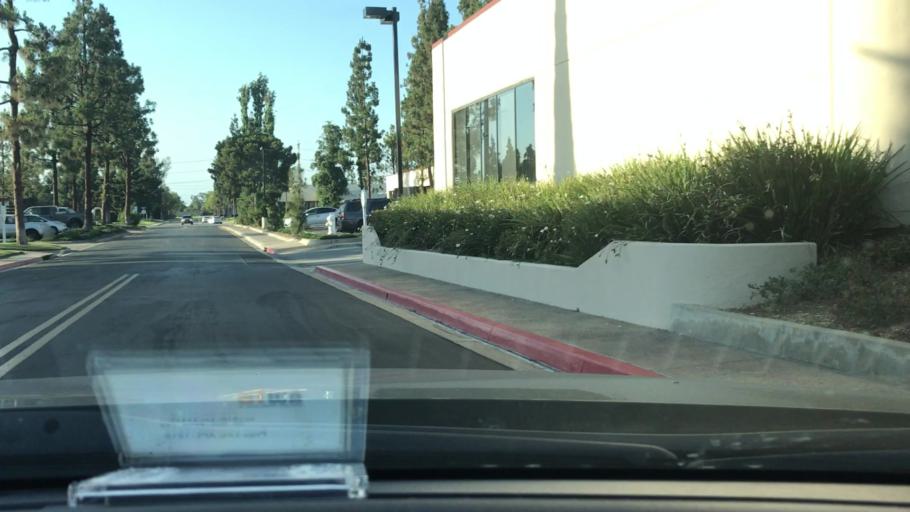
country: US
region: California
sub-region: Orange County
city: Fountain Valley
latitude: 33.6979
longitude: -117.9239
